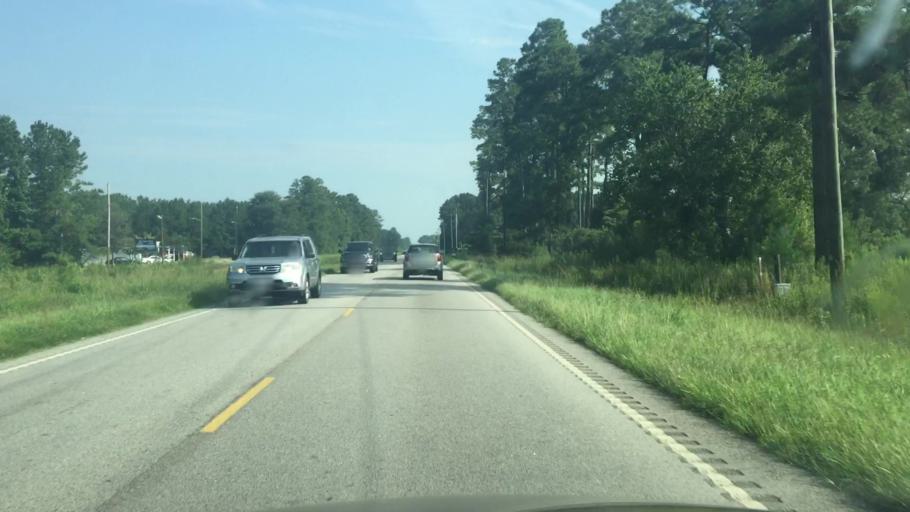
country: US
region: North Carolina
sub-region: Columbus County
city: Tabor City
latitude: 34.1199
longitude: -78.8758
